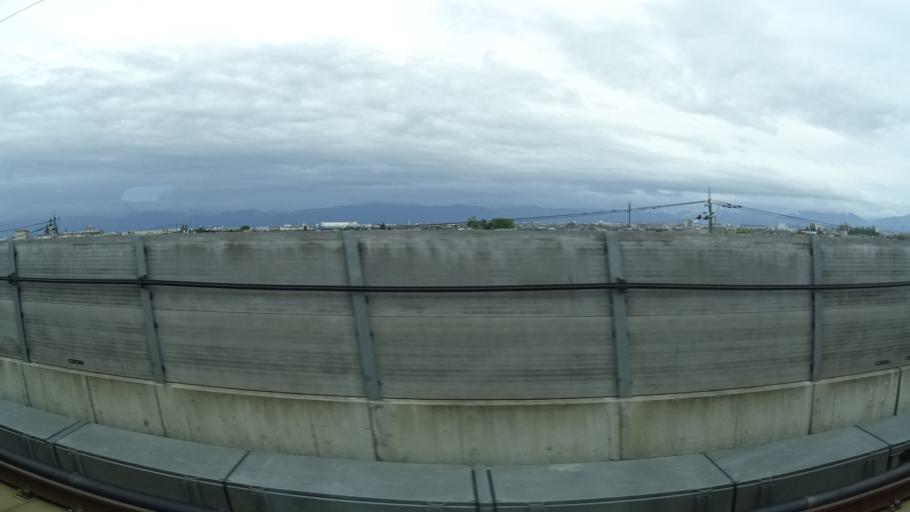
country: JP
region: Toyama
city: Toyama-shi
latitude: 36.7112
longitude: 137.2400
